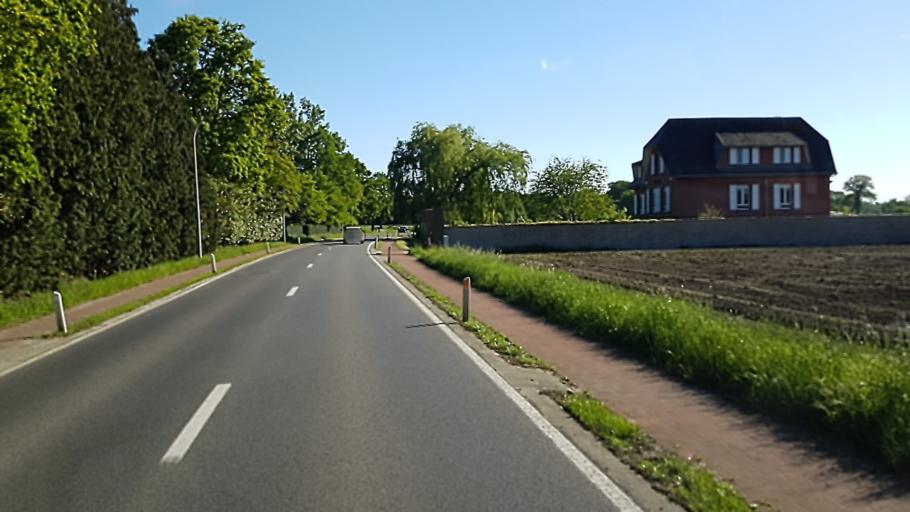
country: BE
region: Flanders
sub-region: Provincie Antwerpen
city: Herenthout
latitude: 51.1166
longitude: 4.7482
